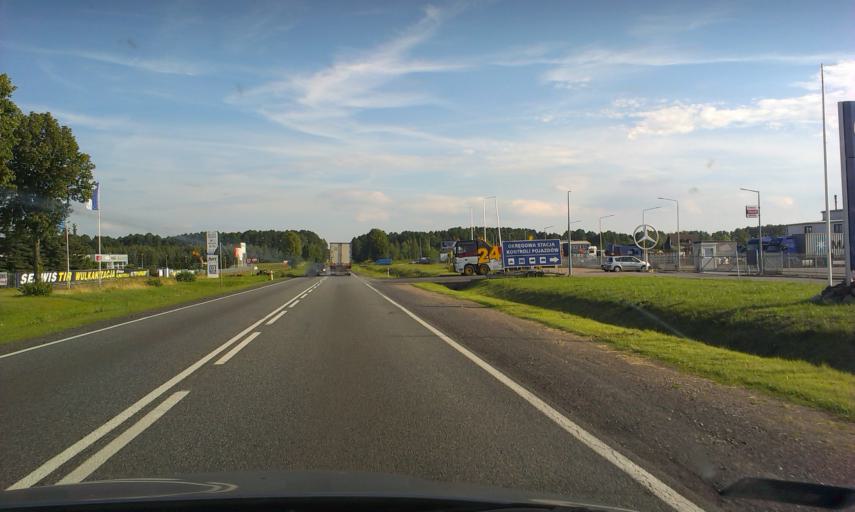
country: PL
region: Kujawsko-Pomorskie
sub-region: Powiat bydgoski
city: Biale Blota
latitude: 53.1335
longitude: 17.8797
